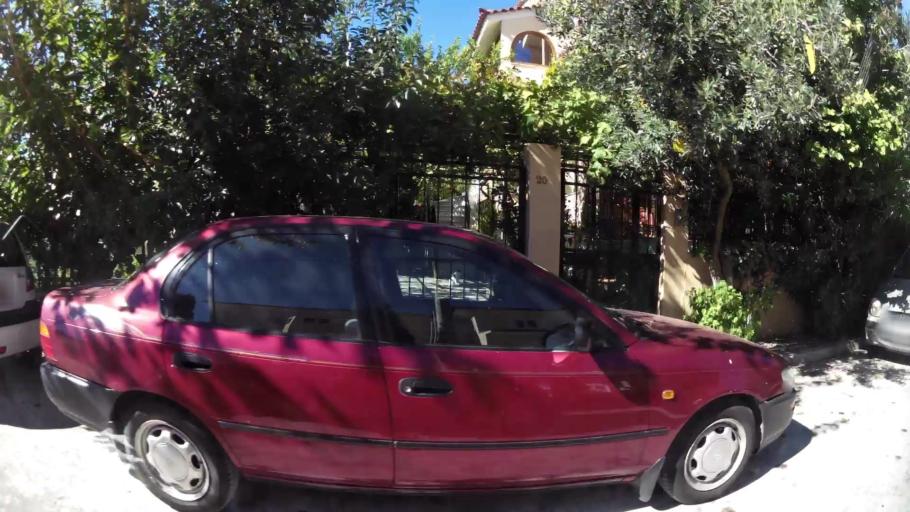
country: GR
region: Attica
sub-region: Nomarchia Anatolikis Attikis
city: Leondarion
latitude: 37.9935
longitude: 23.8584
